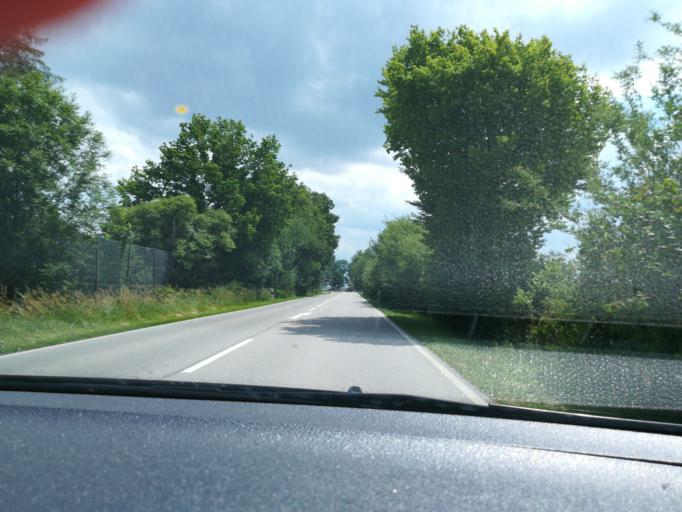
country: DE
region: Bavaria
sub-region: Upper Bavaria
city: Hohenkirchen-Siegertsbrunn
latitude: 48.0234
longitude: 11.7012
